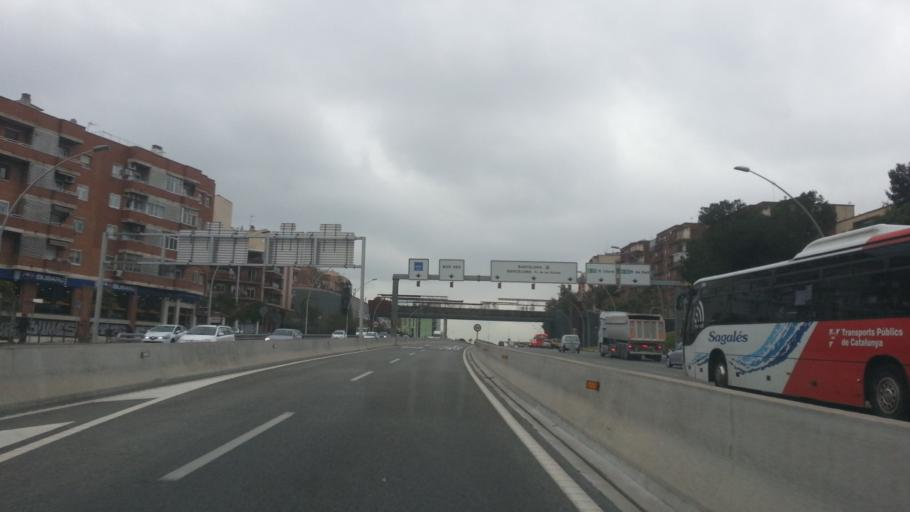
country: ES
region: Catalonia
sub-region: Provincia de Barcelona
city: Nou Barris
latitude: 41.4532
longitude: 2.1888
